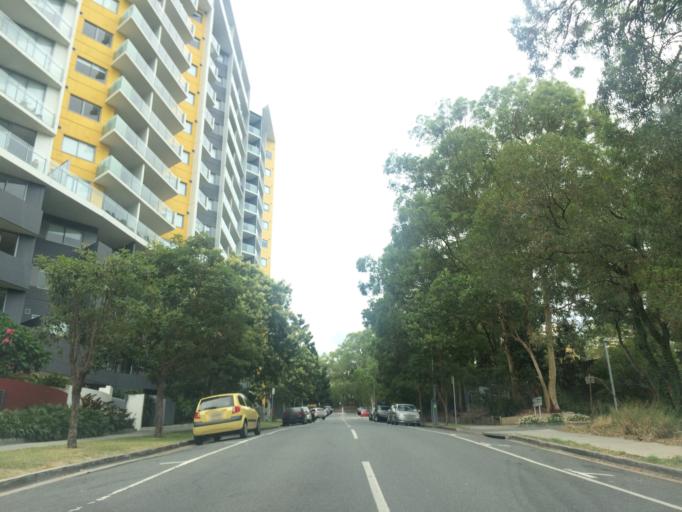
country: AU
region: Queensland
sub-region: Brisbane
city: Spring Hill
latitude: -27.4538
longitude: 153.0160
